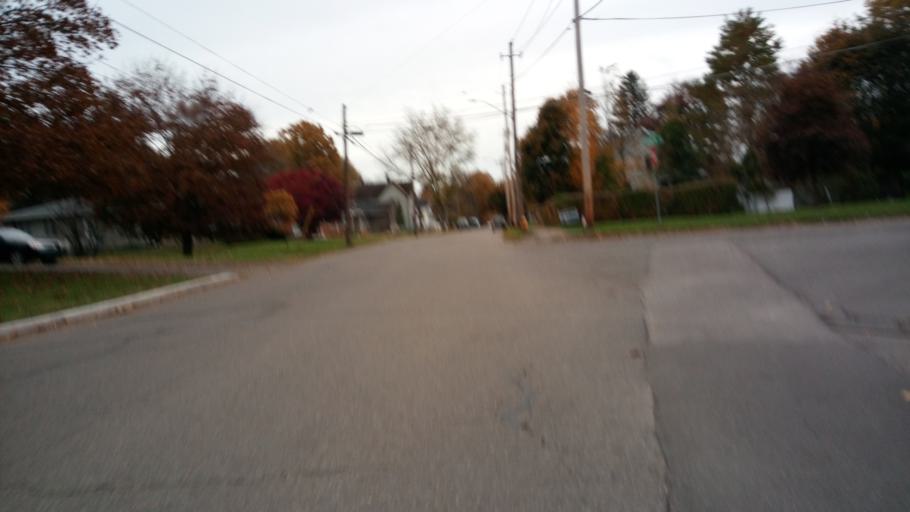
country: US
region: New York
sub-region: Chemung County
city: Elmira
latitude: 42.0844
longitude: -76.7908
